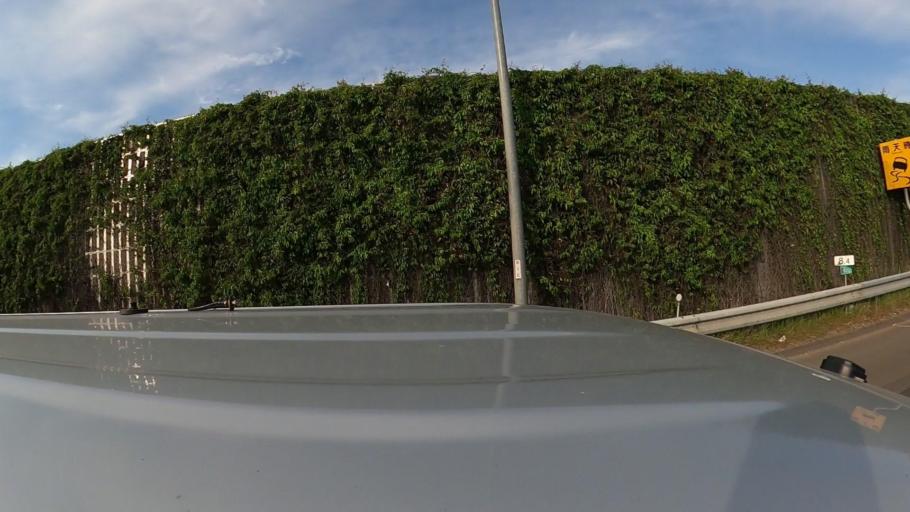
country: JP
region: Saitama
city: Oi
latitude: 35.8020
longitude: 139.5376
